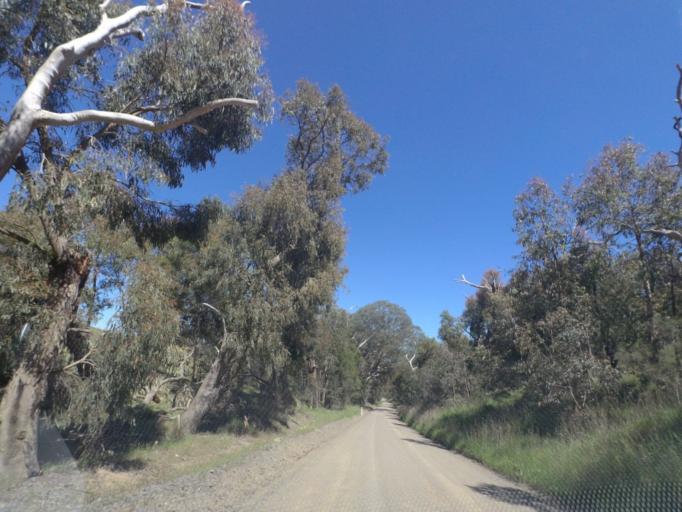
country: AU
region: Victoria
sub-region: Whittlesea
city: Whittlesea
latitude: -37.2833
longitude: 145.0063
